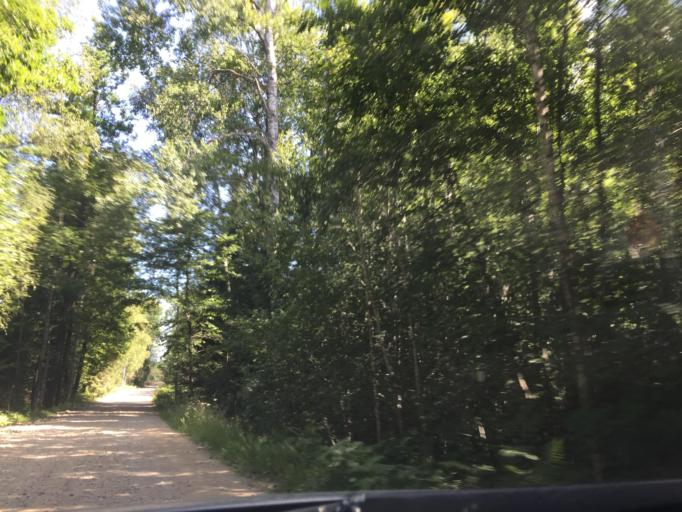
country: LV
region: Talsu Rajons
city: Stende
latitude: 57.1899
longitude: 22.3267
